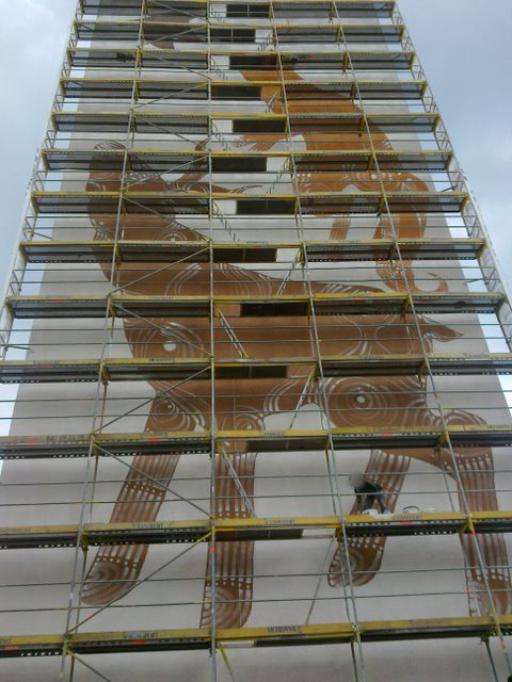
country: PL
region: Pomeranian Voivodeship
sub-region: Sopot
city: Sopot
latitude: 54.3923
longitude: 18.5904
